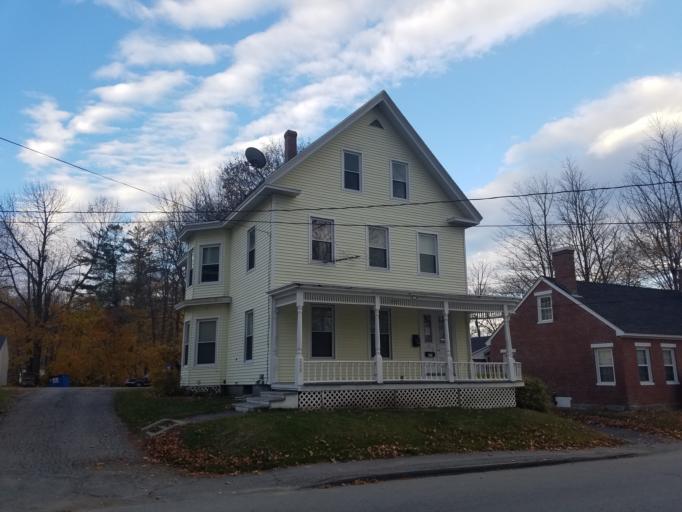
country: US
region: Maine
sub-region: Waldo County
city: Belfast
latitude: 44.4281
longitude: -69.0116
